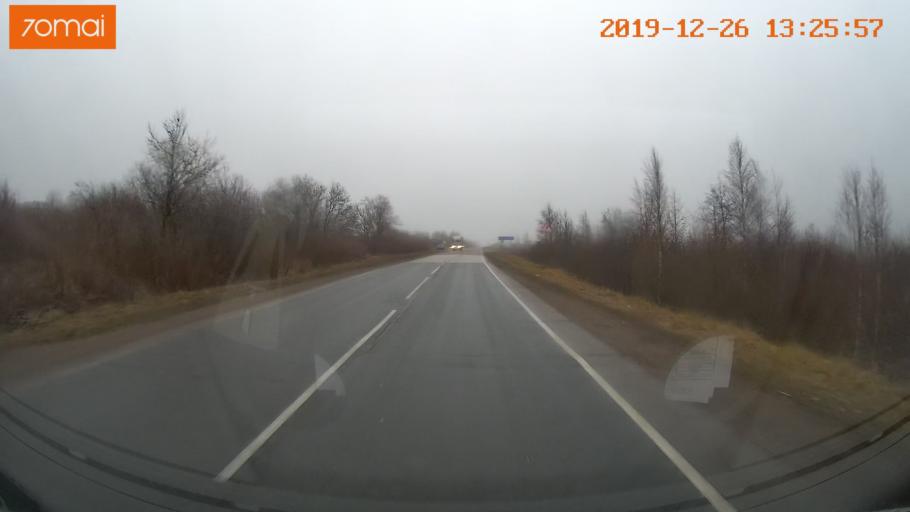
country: RU
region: Vologda
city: Cherepovets
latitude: 58.8699
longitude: 38.2180
